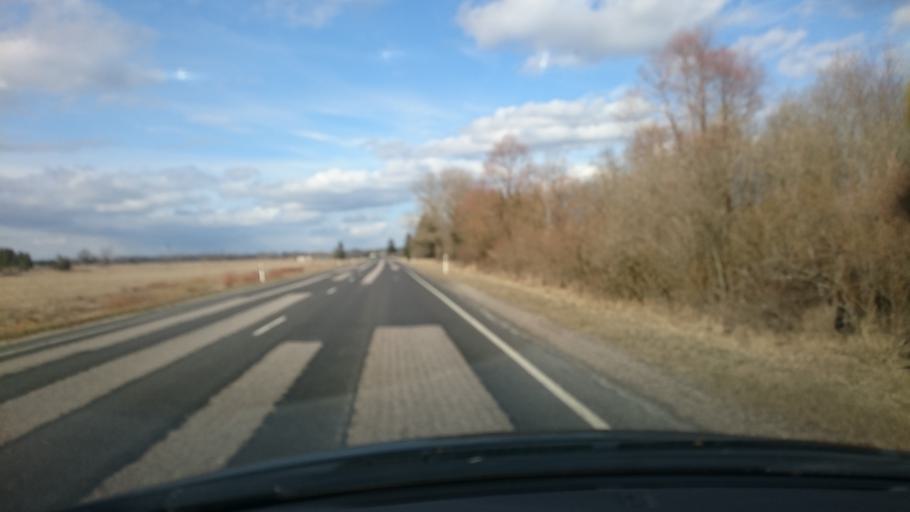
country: EE
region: Harju
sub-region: Nissi vald
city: Turba
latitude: 58.8700
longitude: 24.0821
